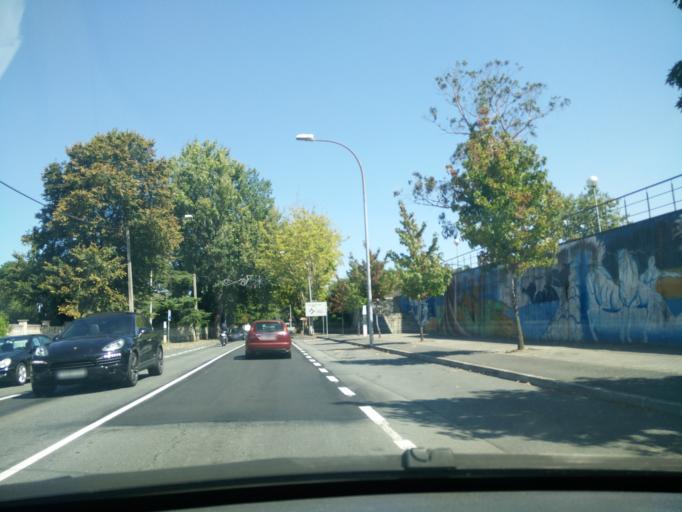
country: ES
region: Galicia
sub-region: Provincia da Coruna
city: A Coruna
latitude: 43.3402
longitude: -8.3712
